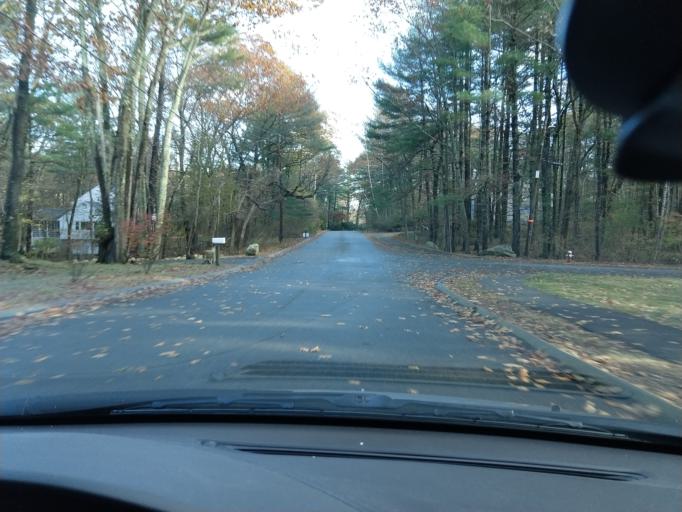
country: US
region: Massachusetts
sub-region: Middlesex County
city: Bedford
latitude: 42.5157
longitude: -71.2684
